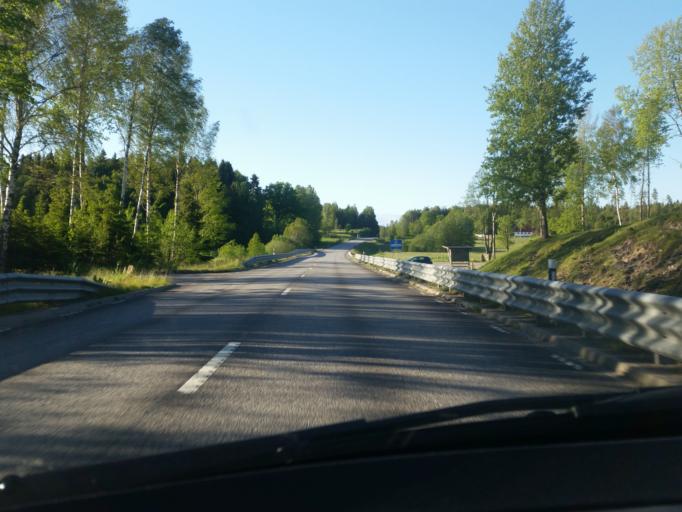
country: SE
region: Vaestra Goetaland
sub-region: Fargelanda Kommun
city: Faergelanda
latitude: 58.5532
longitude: 11.9931
